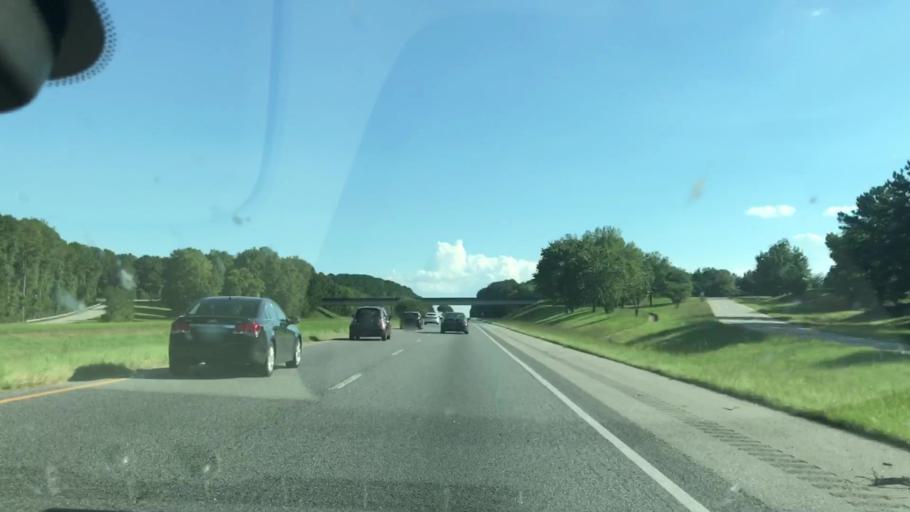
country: US
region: Georgia
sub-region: Harris County
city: Hamilton
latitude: 32.8167
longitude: -85.0213
